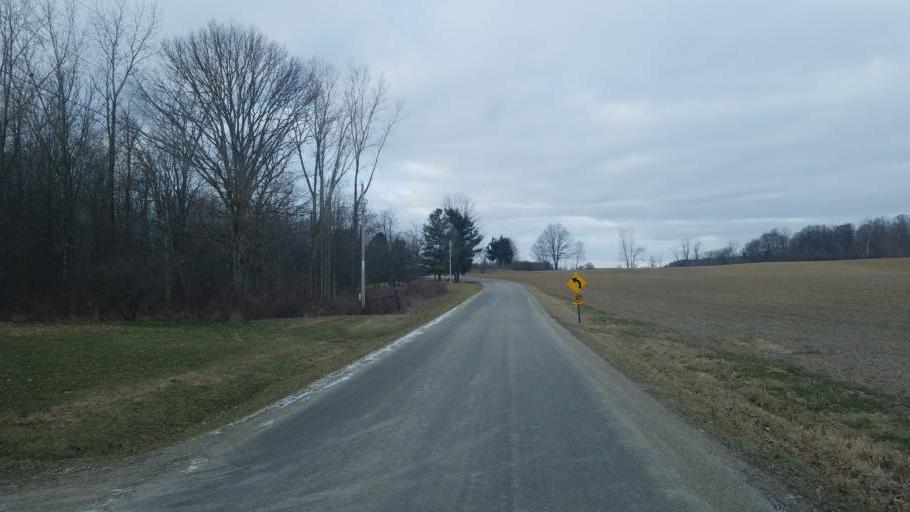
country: US
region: Ohio
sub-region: Morrow County
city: Mount Gilead
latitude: 40.5361
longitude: -82.8026
